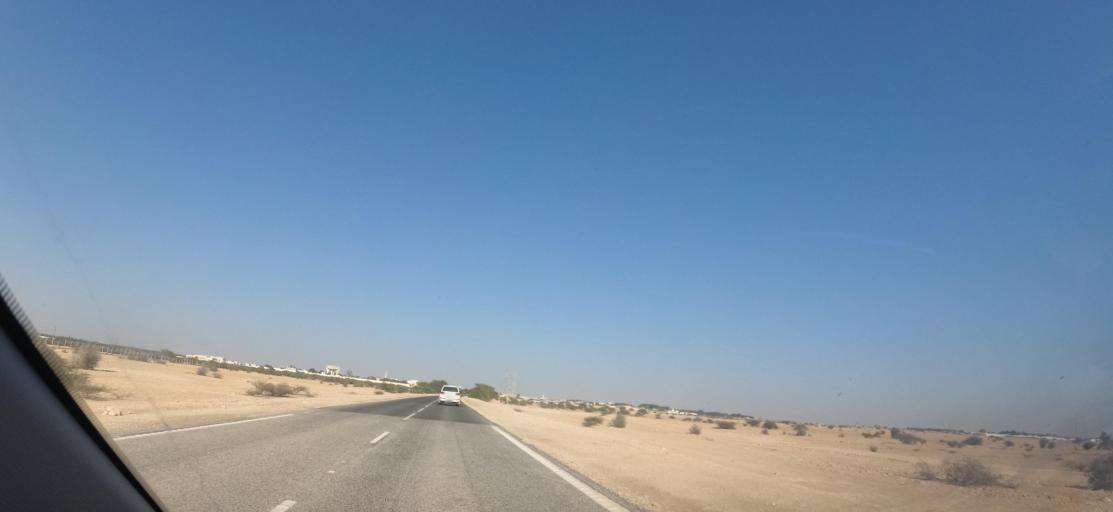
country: QA
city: Al Ghuwayriyah
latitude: 25.8211
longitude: 51.2382
